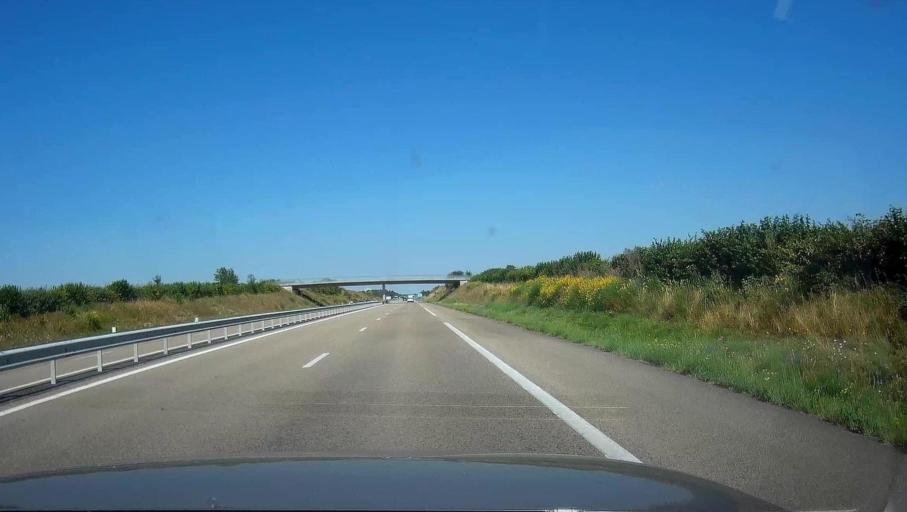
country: FR
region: Champagne-Ardenne
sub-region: Departement de l'Aube
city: Creney-pres-Troyes
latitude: 48.3959
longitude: 4.1519
